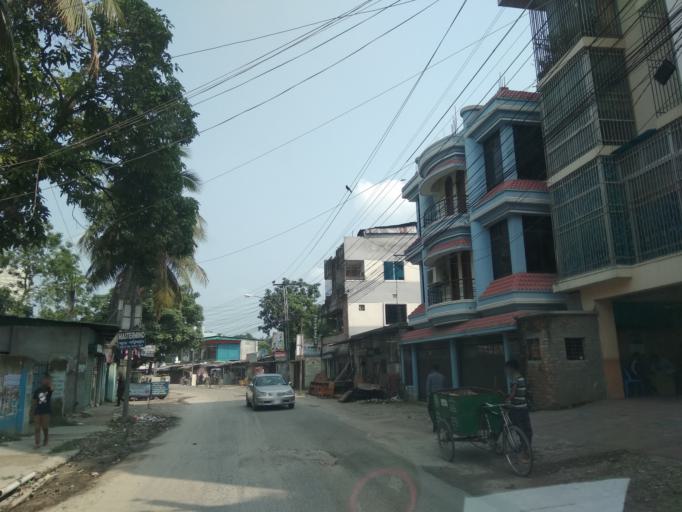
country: BD
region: Rangpur Division
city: Rangpur
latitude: 25.7595
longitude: 89.2327
